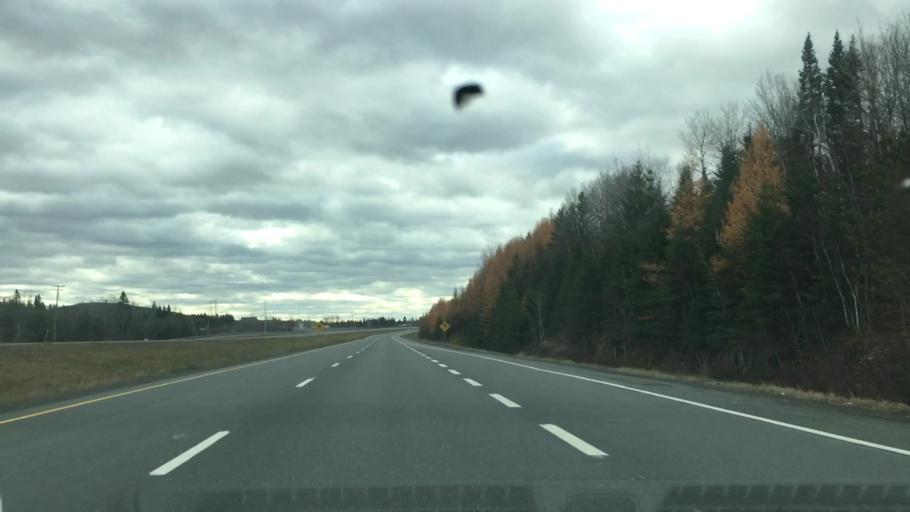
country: US
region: Maine
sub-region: Aroostook County
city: Fort Fairfield
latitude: 46.7467
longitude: -67.7149
